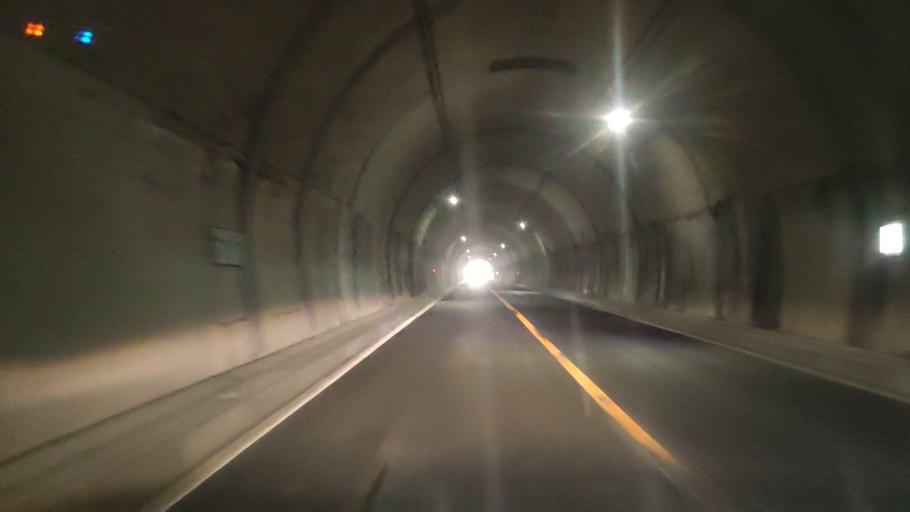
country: JP
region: Oita
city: Saiki
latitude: 32.8832
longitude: 131.9464
